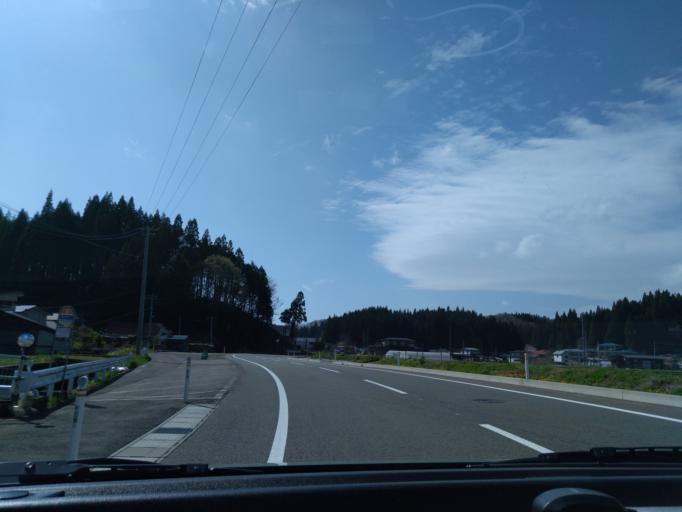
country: JP
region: Akita
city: Akita
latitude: 39.7130
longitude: 140.2005
